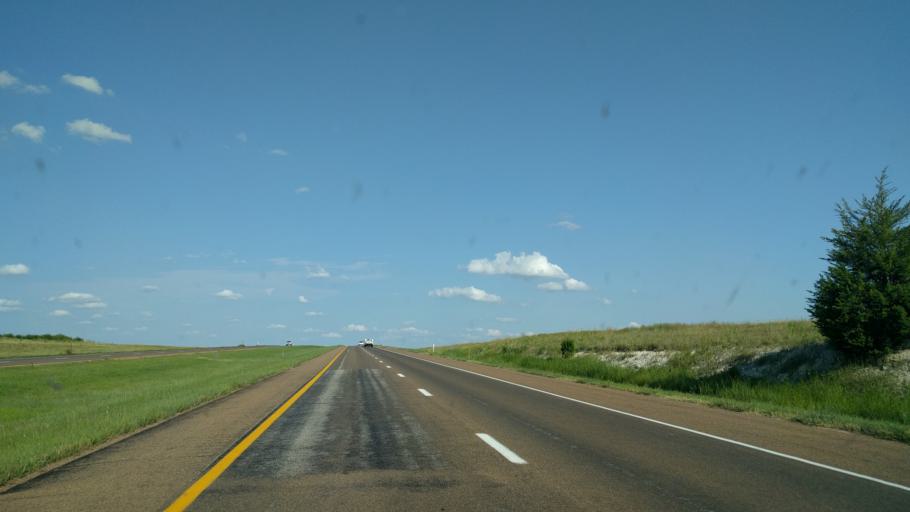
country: US
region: Kansas
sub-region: Ellis County
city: Ellis
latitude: 38.9397
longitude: -99.4886
